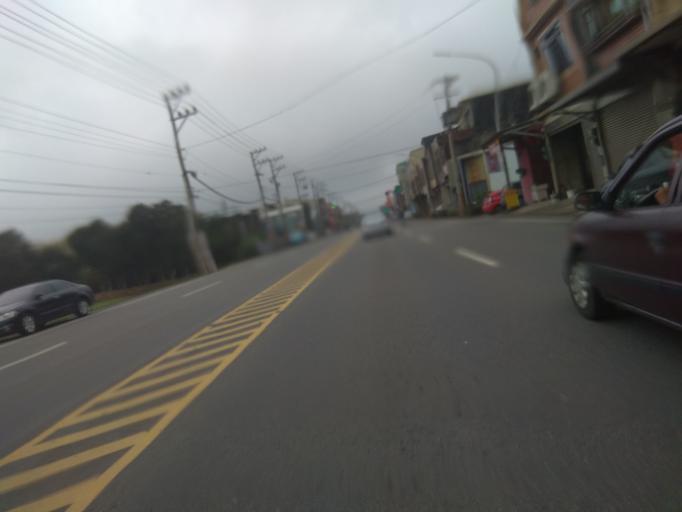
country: TW
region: Taiwan
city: Taoyuan City
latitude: 25.0293
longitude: 121.1066
